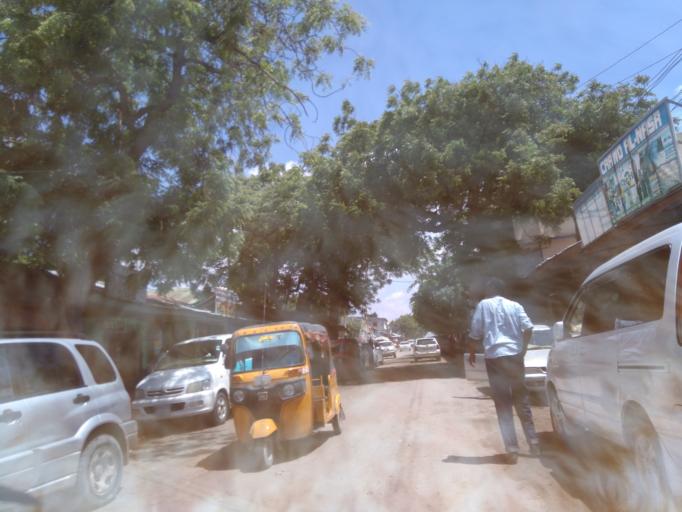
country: SO
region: Banaadir
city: Mogadishu
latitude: 2.0287
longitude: 45.3195
